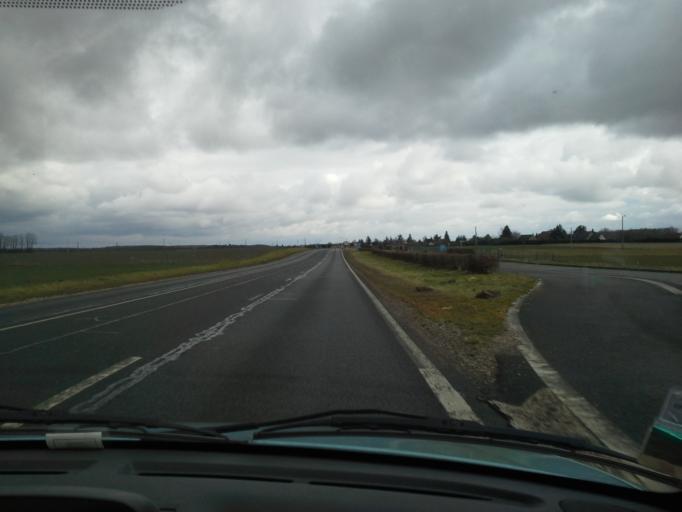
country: FR
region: Centre
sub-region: Departement du Loir-et-Cher
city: Saint-Sulpice-de-Pommeray
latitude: 47.6630
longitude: 1.2564
